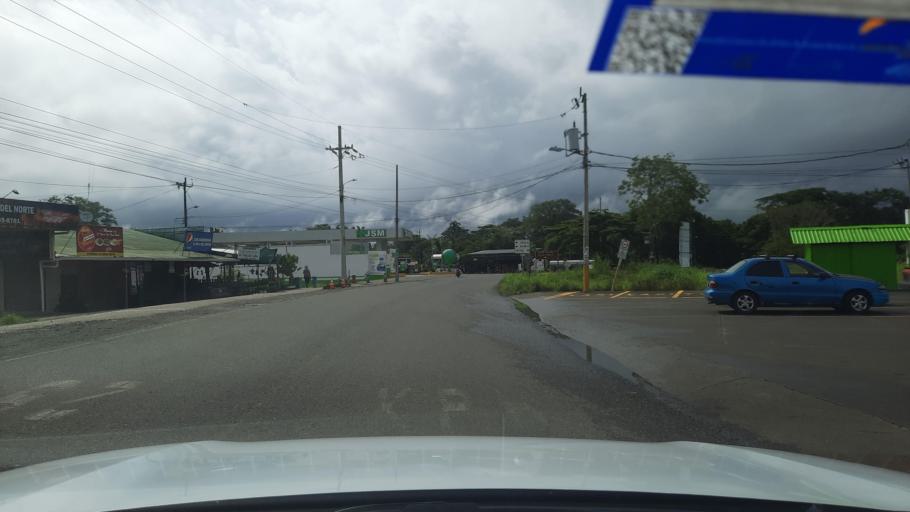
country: CR
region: Alajuela
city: Upala
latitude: 10.8953
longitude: -85.0279
